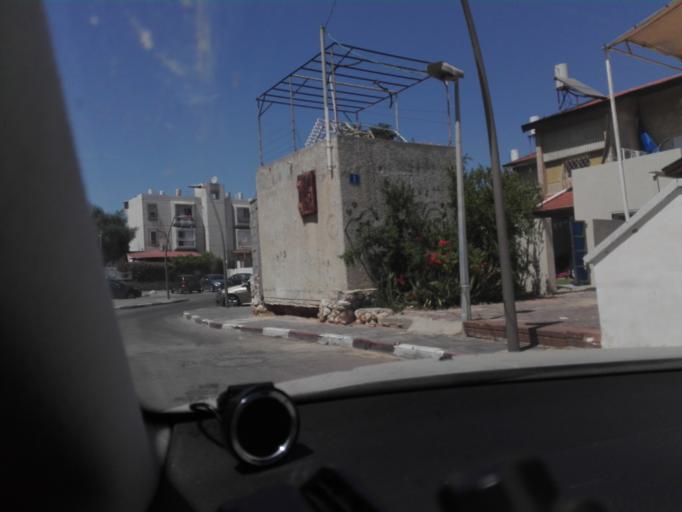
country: IL
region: Central District
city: Bene 'Ayish
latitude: 31.7355
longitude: 34.7462
